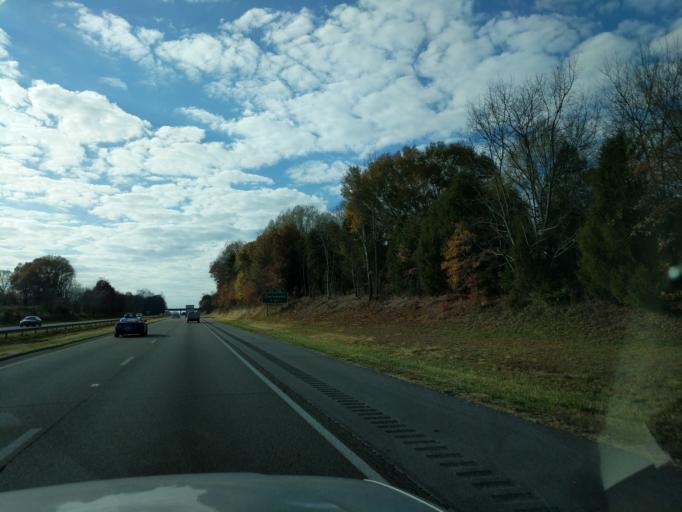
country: US
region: North Carolina
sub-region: Catawba County
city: Claremont
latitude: 35.7265
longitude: -81.1352
